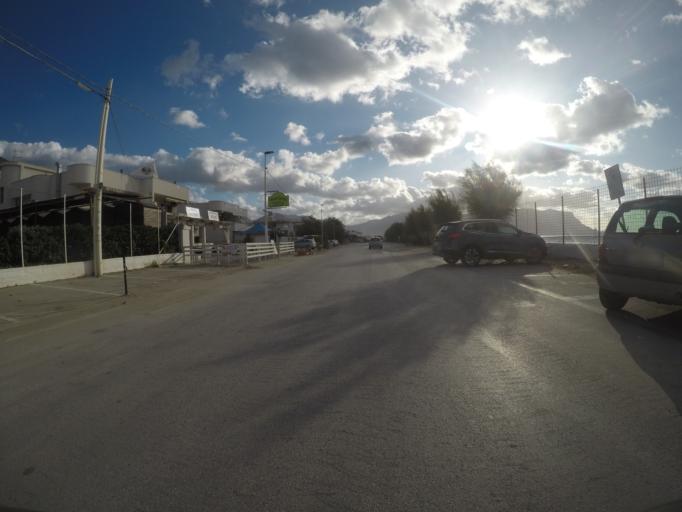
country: IT
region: Sicily
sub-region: Palermo
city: Isola delle Femmine
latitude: 38.1873
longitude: 13.2399
